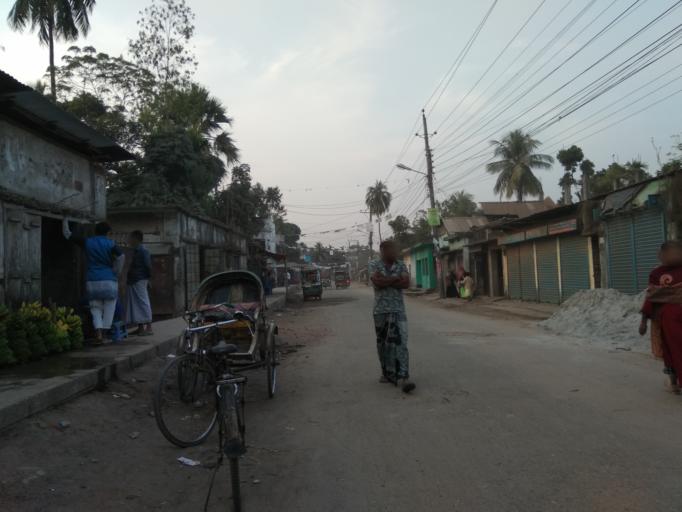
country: BD
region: Rangpur Division
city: Rangpur
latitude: 25.7306
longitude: 89.2628
